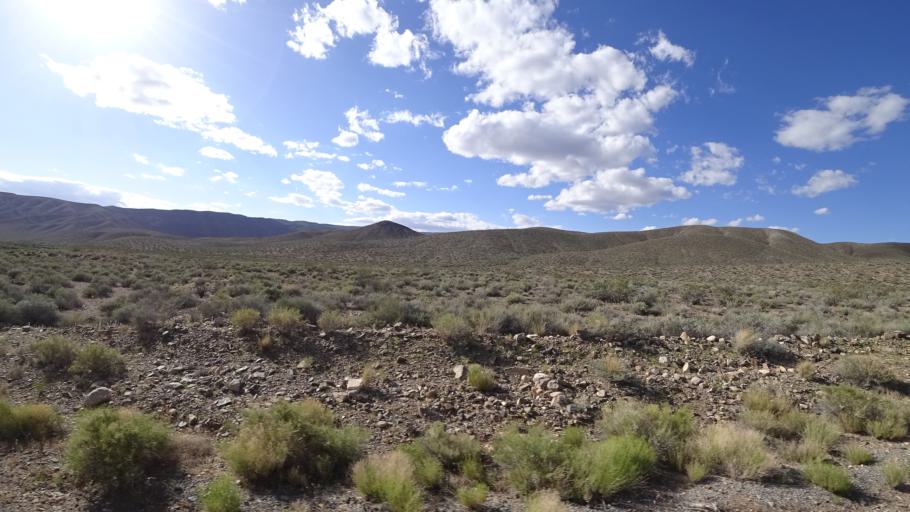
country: US
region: California
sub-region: San Bernardino County
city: Searles Valley
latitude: 36.3018
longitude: -117.1672
